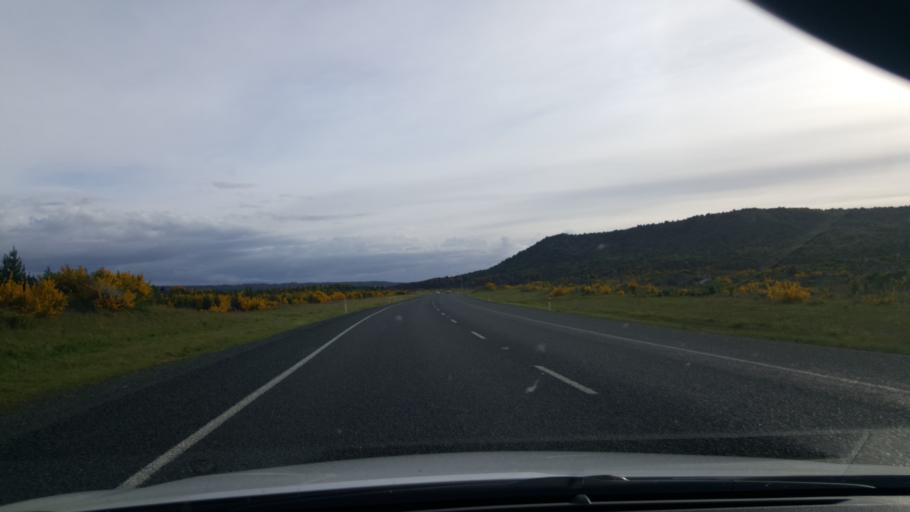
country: NZ
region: Waikato
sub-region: Taupo District
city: Taupo
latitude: -38.8400
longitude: 176.0631
